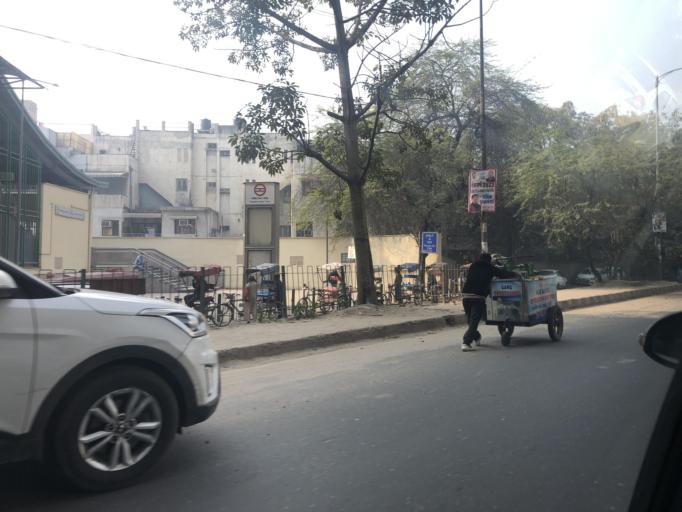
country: IN
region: NCT
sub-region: North West Delhi
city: Pitampura
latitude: 28.6785
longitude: 77.1020
